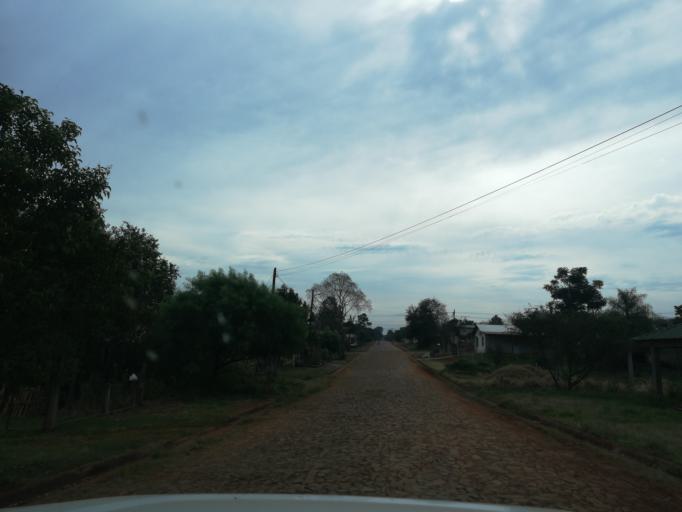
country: AR
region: Misiones
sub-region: Departamento de San Pedro
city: San Pedro
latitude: -26.6271
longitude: -54.1050
